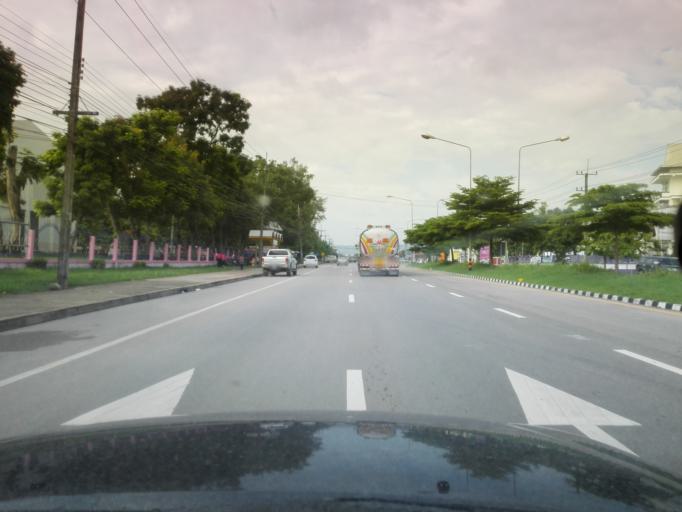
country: TH
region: Tak
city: Mae Sot
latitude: 16.7137
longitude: 98.5551
